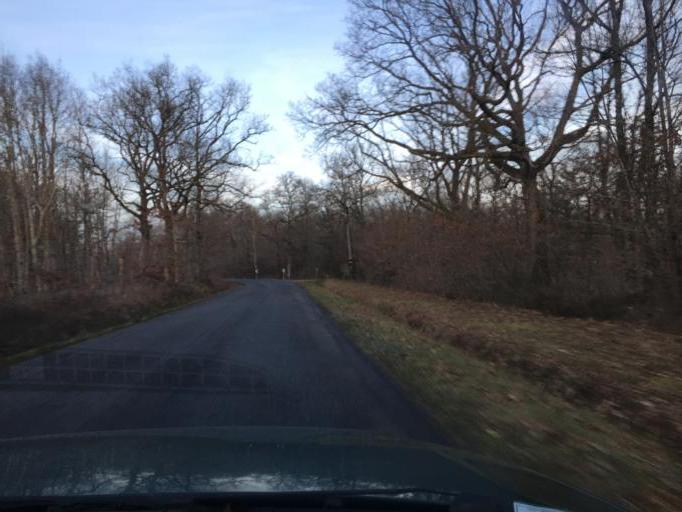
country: FR
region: Centre
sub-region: Departement du Loiret
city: Olivet
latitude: 47.7937
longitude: 1.8968
